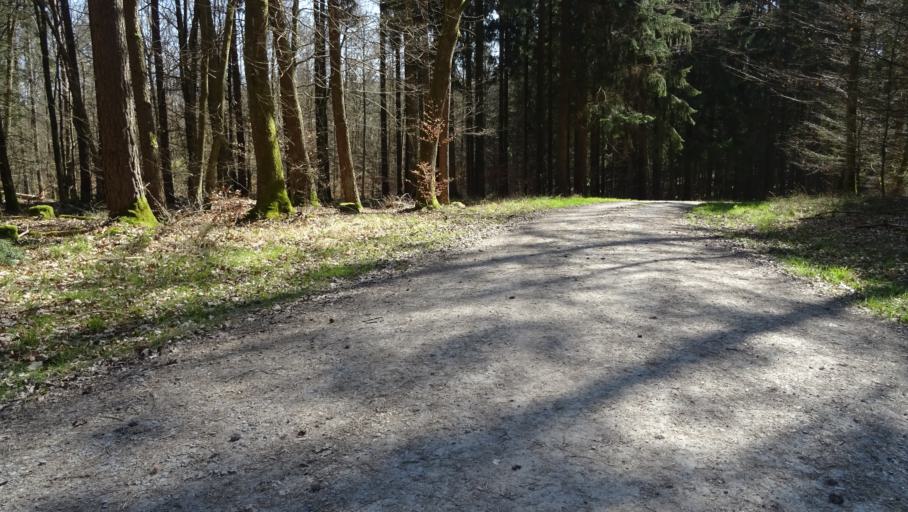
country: DE
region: Baden-Wuerttemberg
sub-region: Regierungsbezirk Stuttgart
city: Roigheim
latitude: 49.4018
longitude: 9.3323
